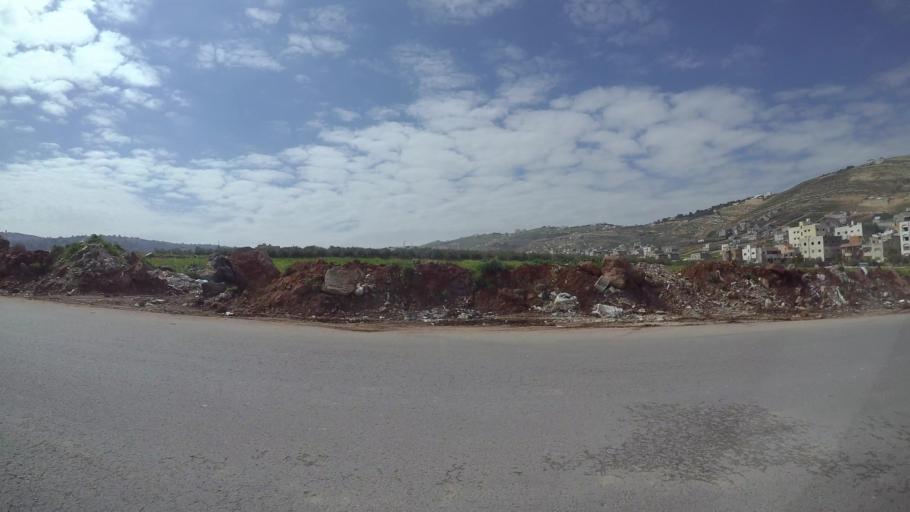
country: JO
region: Amman
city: Al Jubayhah
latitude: 32.0665
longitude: 35.8182
